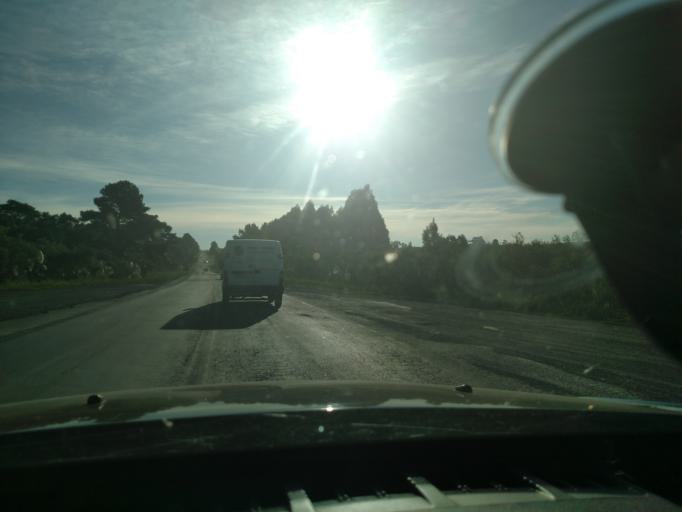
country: BR
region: Santa Catarina
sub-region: Lages
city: Lages
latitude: -27.7812
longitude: -50.2472
